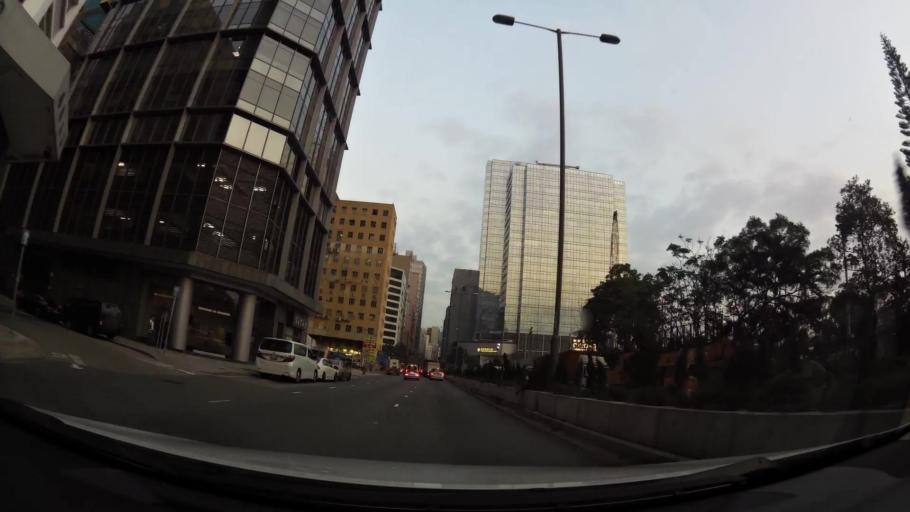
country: HK
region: Kowloon City
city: Kowloon
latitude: 22.3151
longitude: 114.2161
